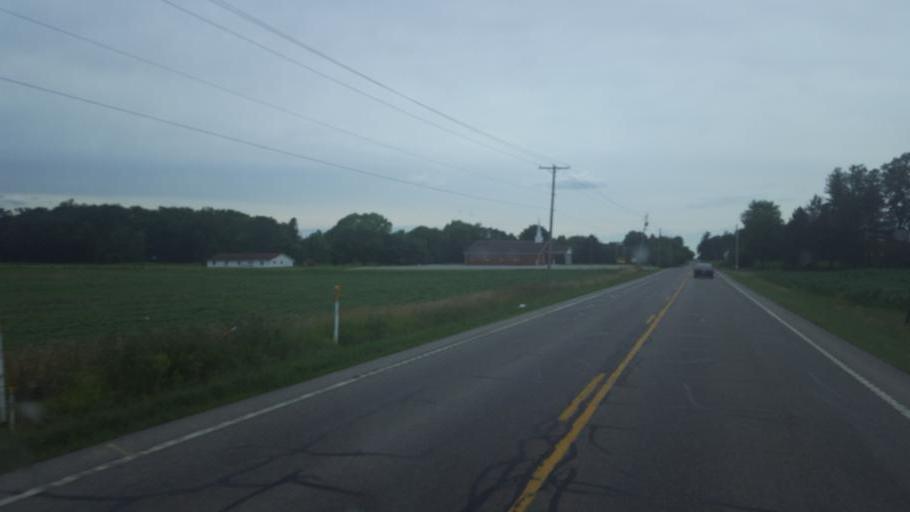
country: US
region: Ohio
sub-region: Richland County
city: Lincoln Heights
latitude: 40.8624
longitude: -82.5134
